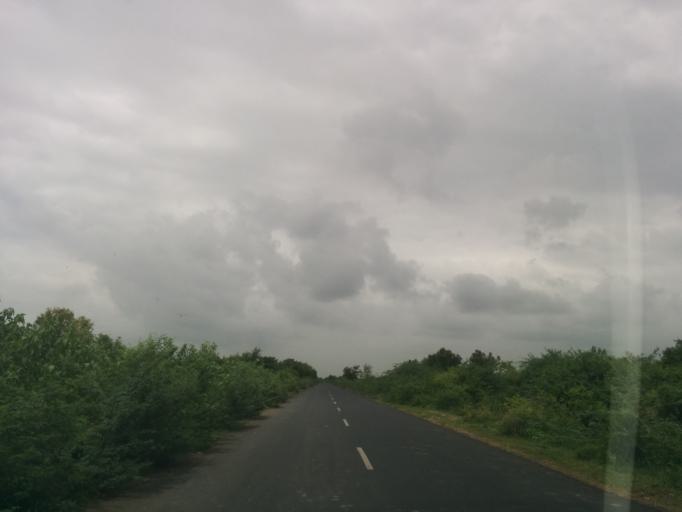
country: IN
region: Gujarat
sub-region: Ahmadabad
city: Sanand
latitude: 23.0791
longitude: 72.4037
